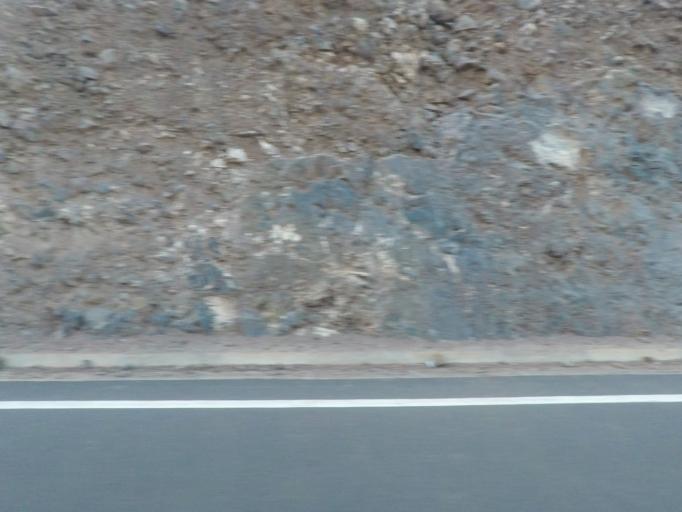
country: ES
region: Canary Islands
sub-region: Provincia de Santa Cruz de Tenerife
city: San Sebastian de la Gomera
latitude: 28.0875
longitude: -17.1277
